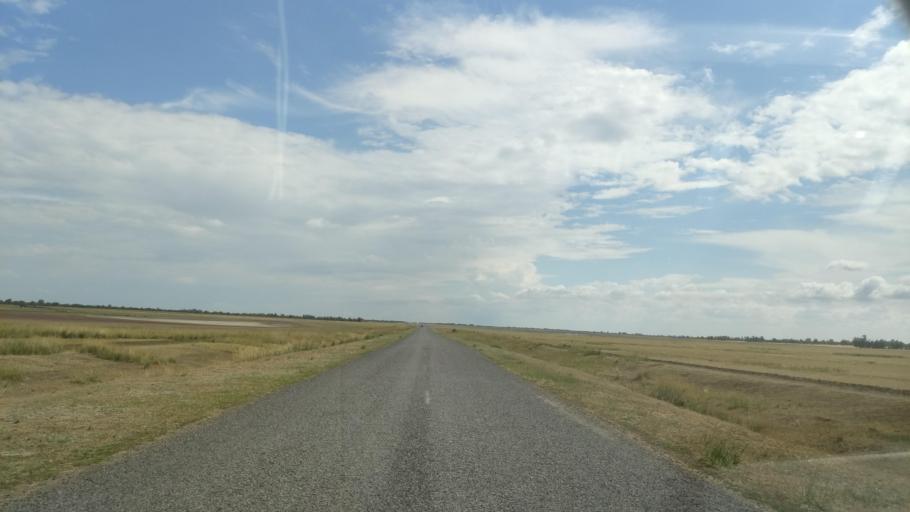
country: KZ
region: Pavlodar
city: Pavlodar
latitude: 52.6354
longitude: 76.9110
